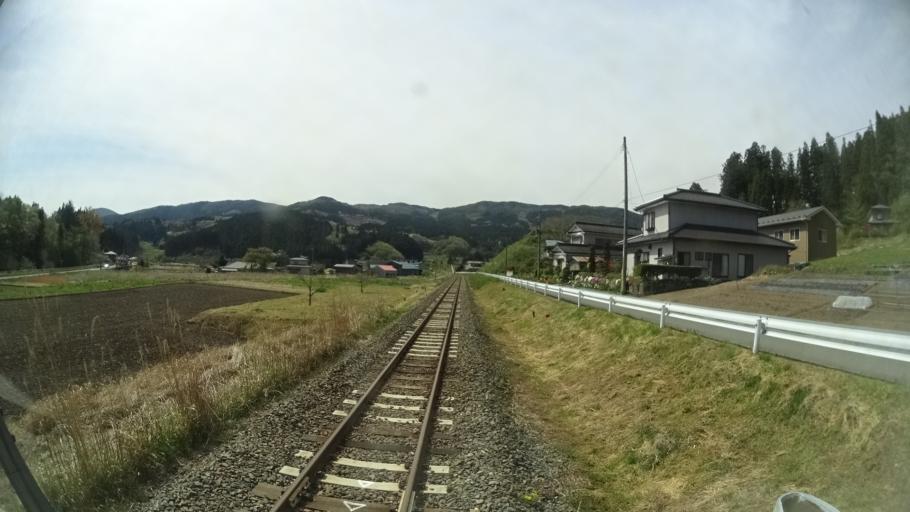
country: JP
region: Iwate
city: Ofunato
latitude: 38.9196
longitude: 141.4642
